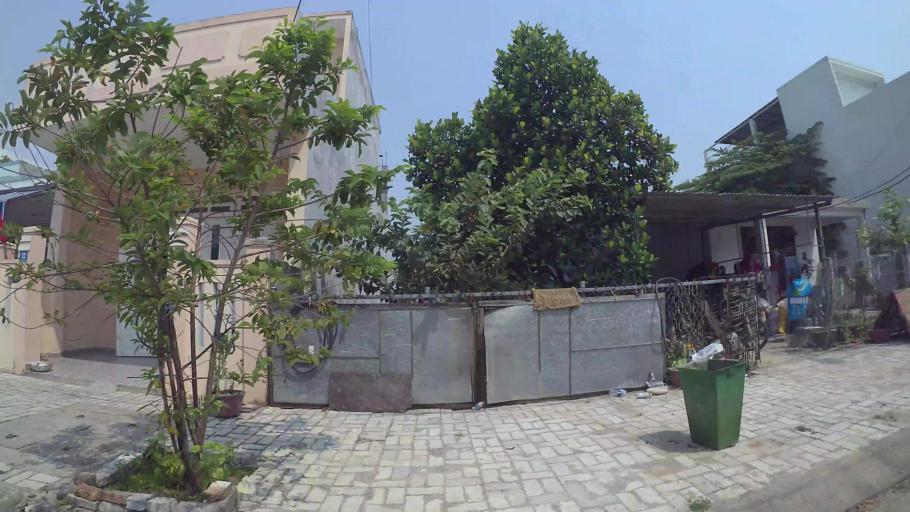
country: VN
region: Da Nang
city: Cam Le
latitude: 15.9843
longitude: 108.2158
